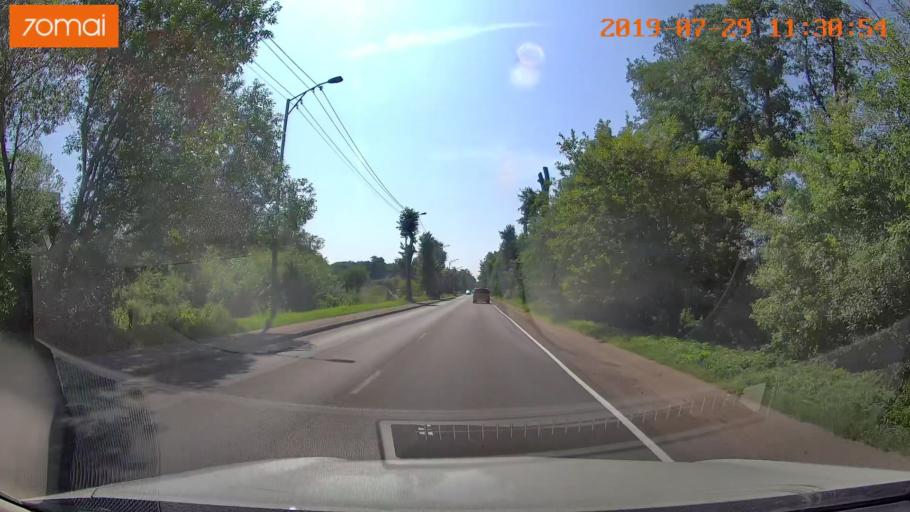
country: RU
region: Kaliningrad
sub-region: Gorod Kaliningrad
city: Kaliningrad
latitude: 54.6790
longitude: 20.5378
